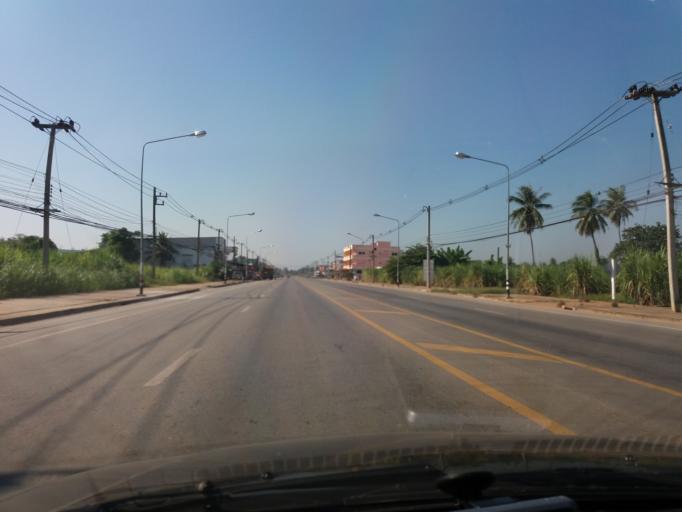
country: TH
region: Kamphaeng Phet
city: Khlong Khlung
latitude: 16.2289
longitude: 99.7323
